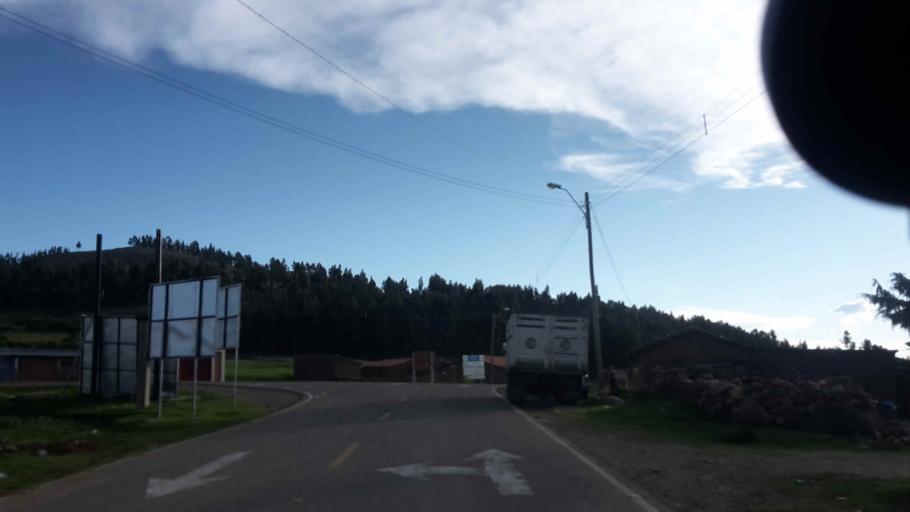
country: BO
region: Cochabamba
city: Arani
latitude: -17.5469
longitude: -65.6723
